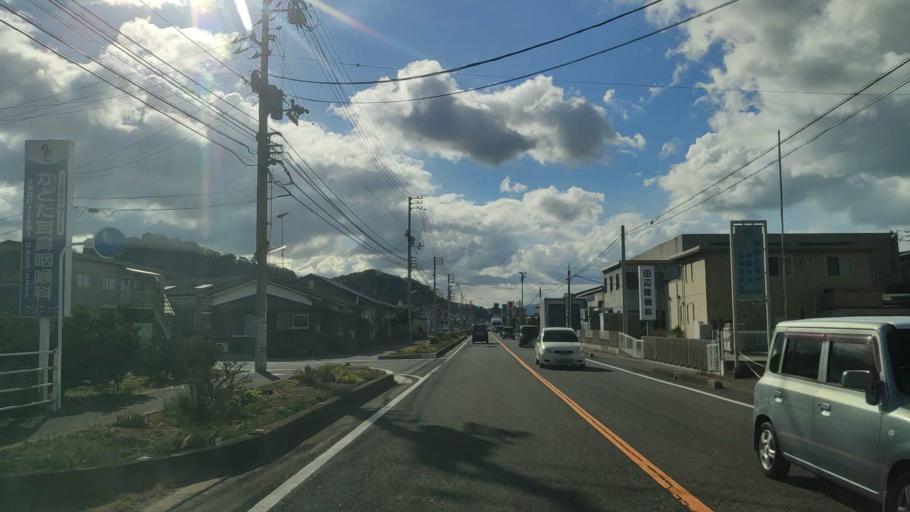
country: JP
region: Ehime
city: Masaki-cho
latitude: 33.8399
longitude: 132.7092
